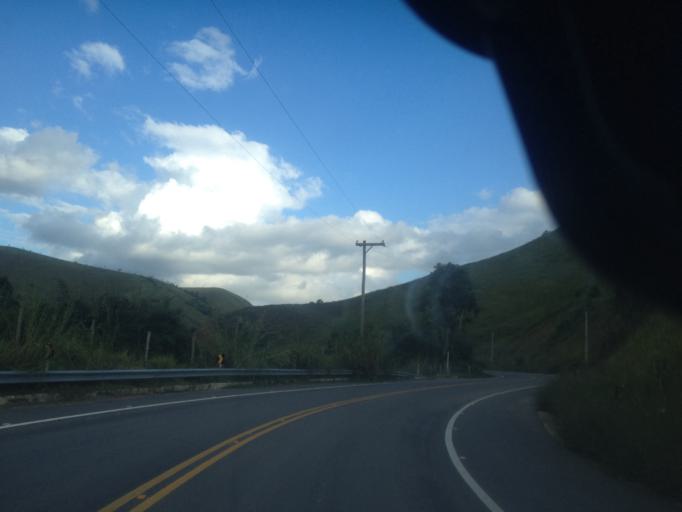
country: BR
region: Rio de Janeiro
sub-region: Quatis
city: Quatis
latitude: -22.2686
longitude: -44.2606
